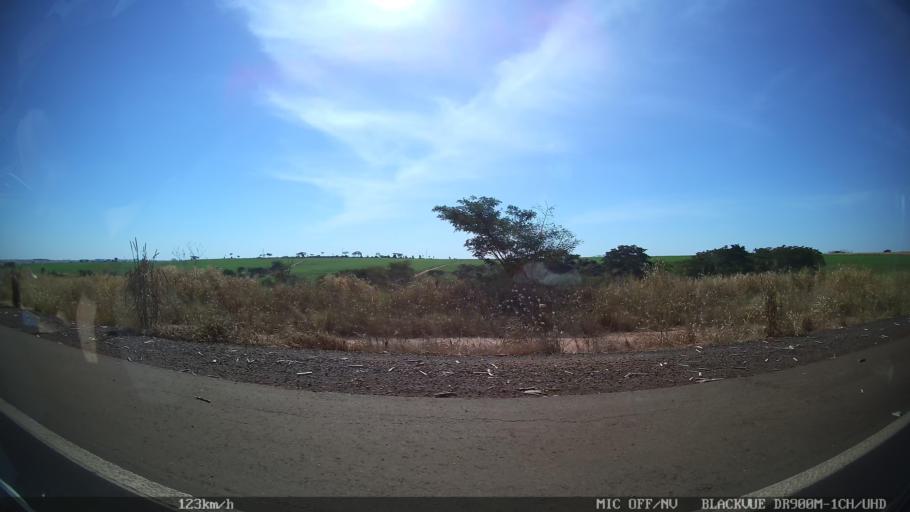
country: BR
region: Sao Paulo
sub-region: Olimpia
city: Olimpia
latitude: -20.6264
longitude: -48.7901
